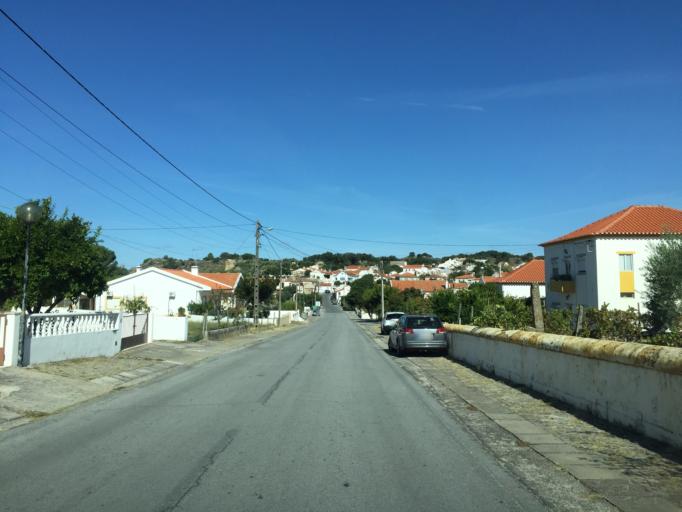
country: PT
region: Portalegre
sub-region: Marvao
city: Marvao
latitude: 39.4450
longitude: -7.3695
